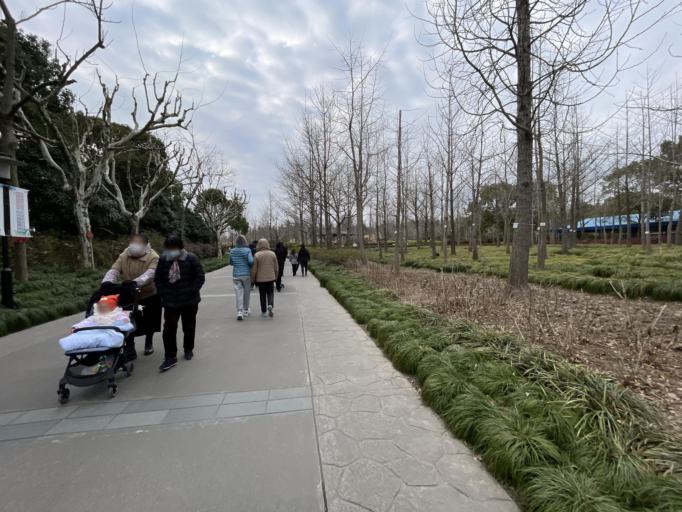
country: CN
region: Shanghai Shi
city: Yangpu
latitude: 31.2972
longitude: 121.5273
